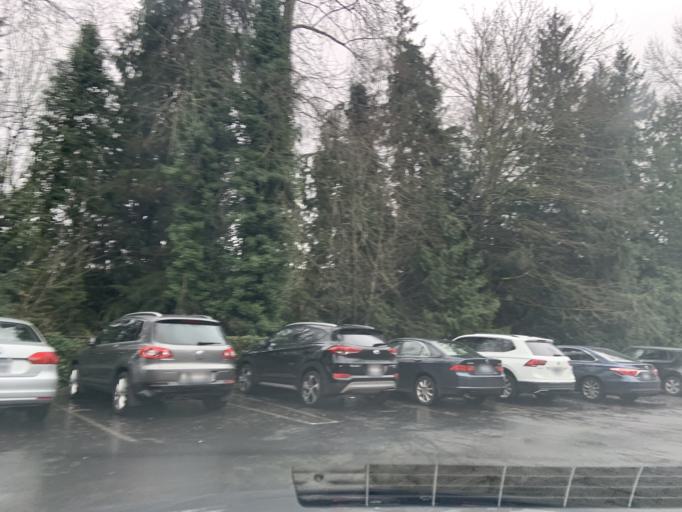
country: US
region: Washington
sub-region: Snohomish County
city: Mountlake Terrace
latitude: 47.7797
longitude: -122.3151
